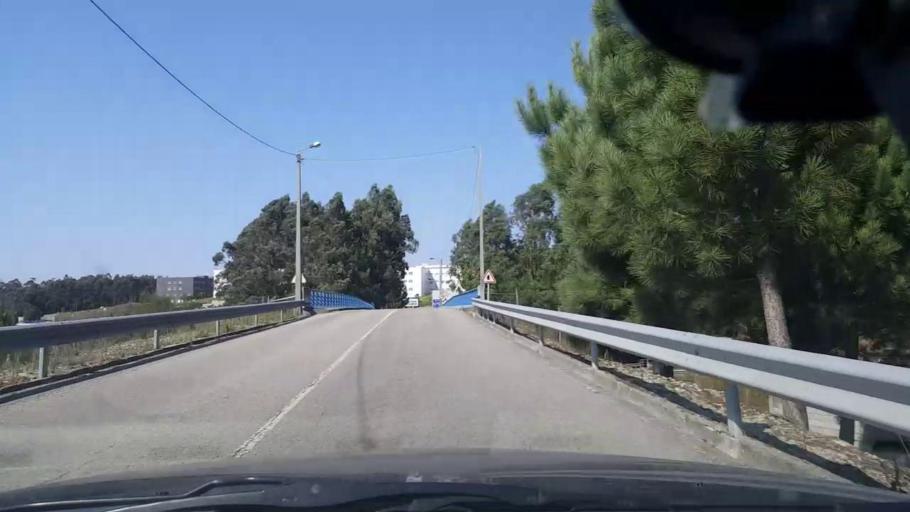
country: PT
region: Porto
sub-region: Vila do Conde
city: Vila do Conde
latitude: 41.3838
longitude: -8.7096
